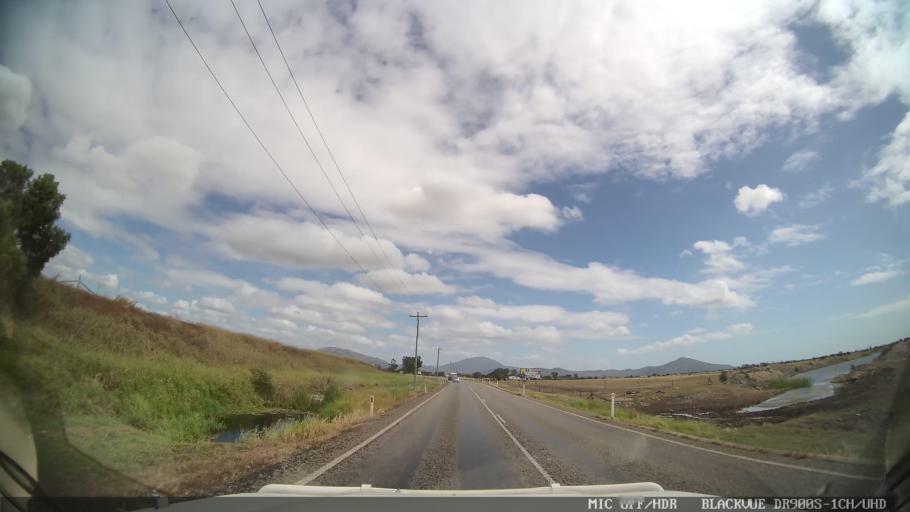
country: AU
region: Queensland
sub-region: Whitsunday
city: Bowen
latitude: -20.0151
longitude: 148.1783
